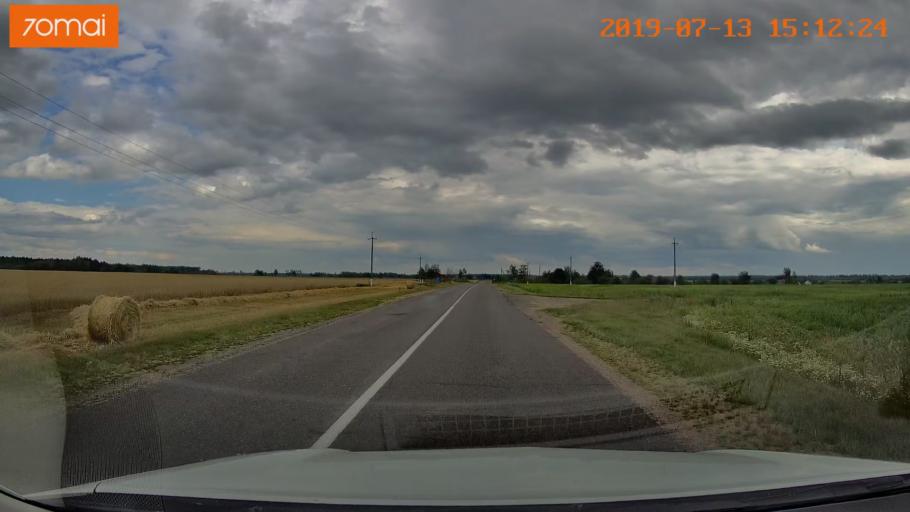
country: BY
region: Mogilev
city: Hlusha
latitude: 53.1490
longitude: 28.7911
